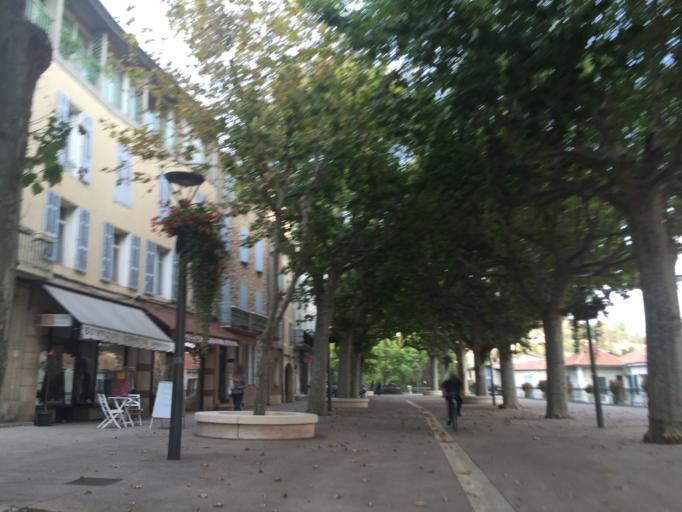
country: FR
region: Provence-Alpes-Cote d'Azur
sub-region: Departement des Alpes-de-Haute-Provence
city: Manosque
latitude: 43.8320
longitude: 5.7845
